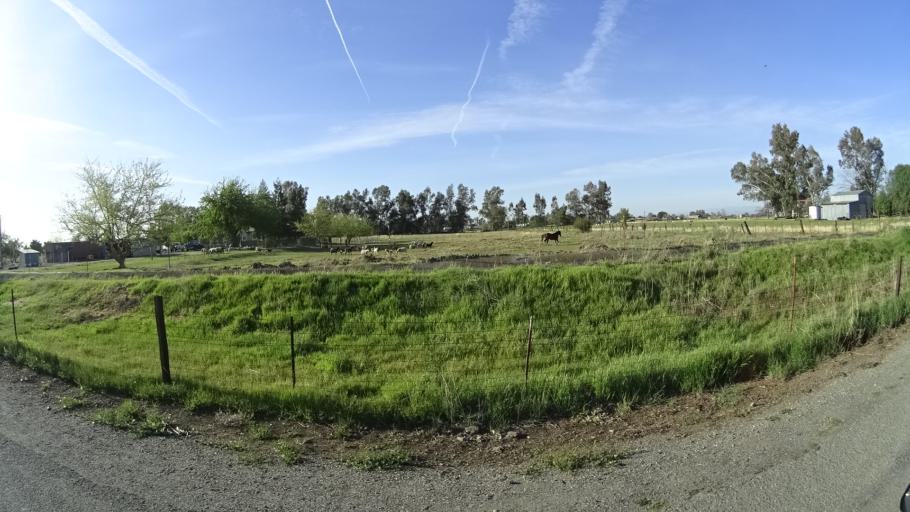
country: US
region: California
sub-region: Glenn County
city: Orland
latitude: 39.7332
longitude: -122.2082
